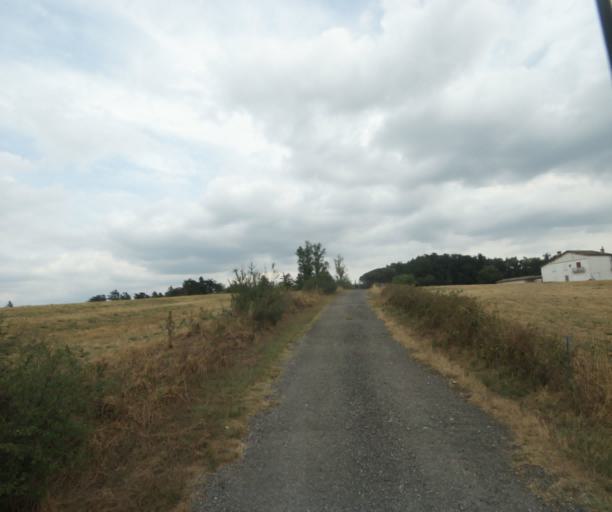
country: FR
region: Midi-Pyrenees
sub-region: Departement de la Haute-Garonne
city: Revel
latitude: 43.4416
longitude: 2.0146
